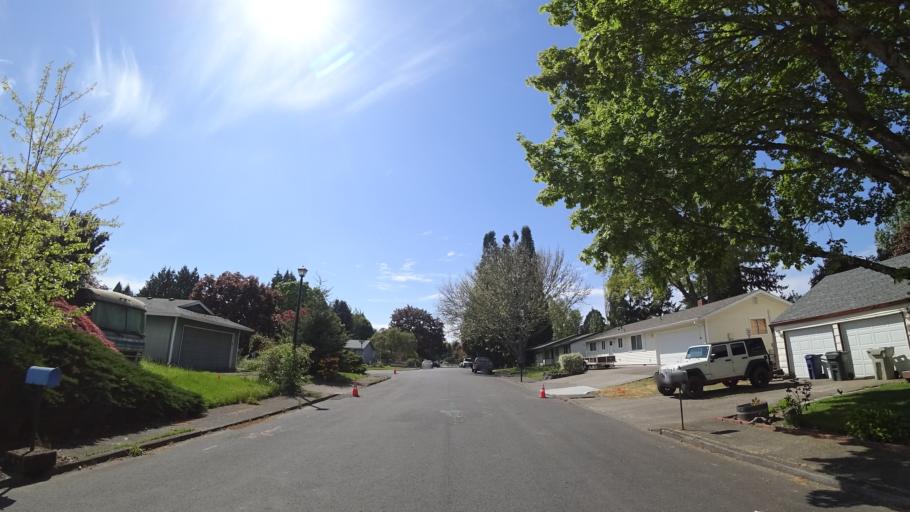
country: US
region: Oregon
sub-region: Washington County
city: Aloha
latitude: 45.4909
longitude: -122.8830
